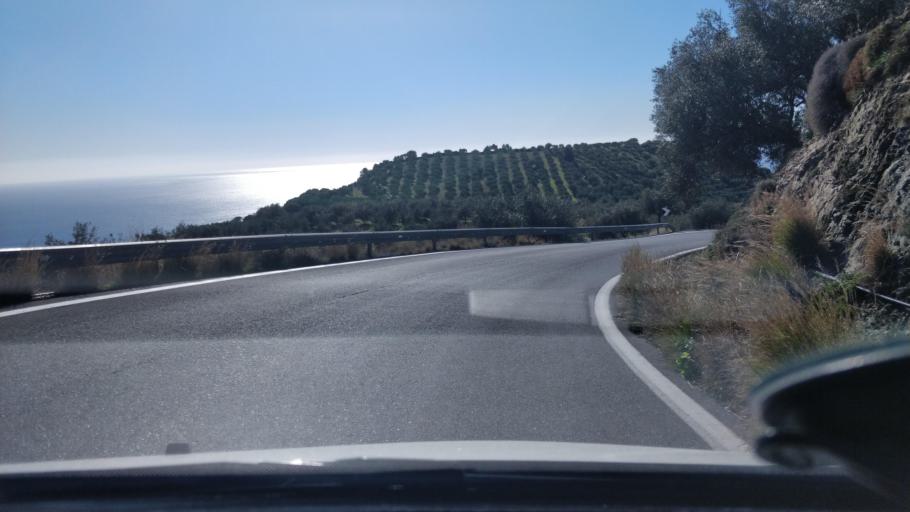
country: GR
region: Crete
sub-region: Nomos Irakleiou
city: Arkalochori
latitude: 35.0078
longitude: 25.4420
